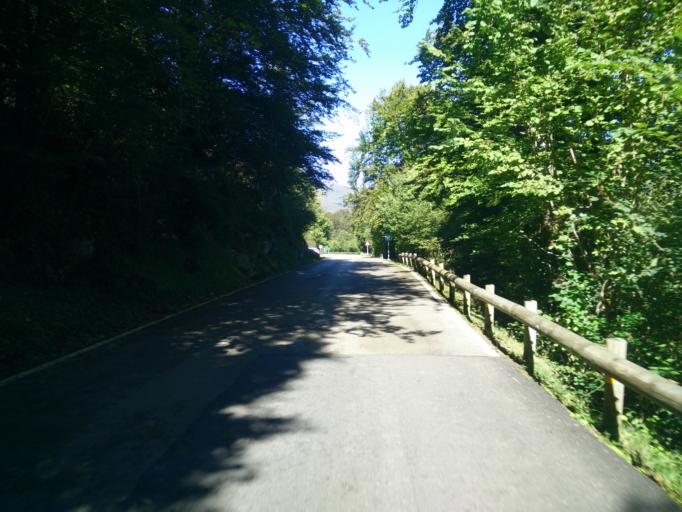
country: ES
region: Cantabria
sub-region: Provincia de Cantabria
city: Ruente
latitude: 43.1119
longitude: -4.2846
